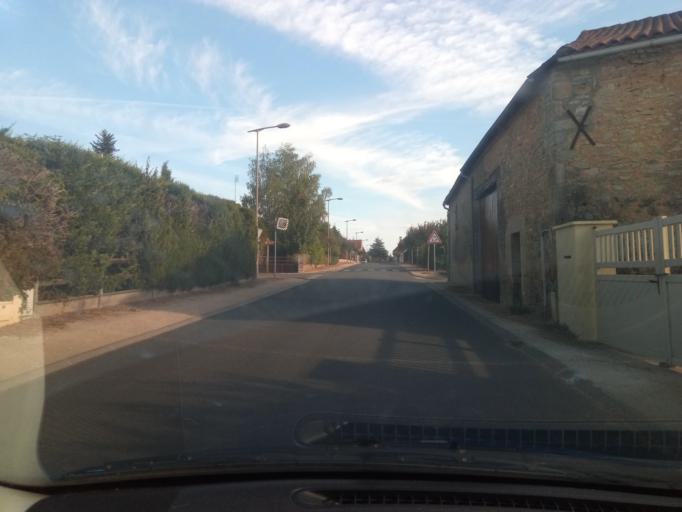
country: FR
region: Poitou-Charentes
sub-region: Departement de la Vienne
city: Montmorillon
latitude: 46.4917
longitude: 0.8406
